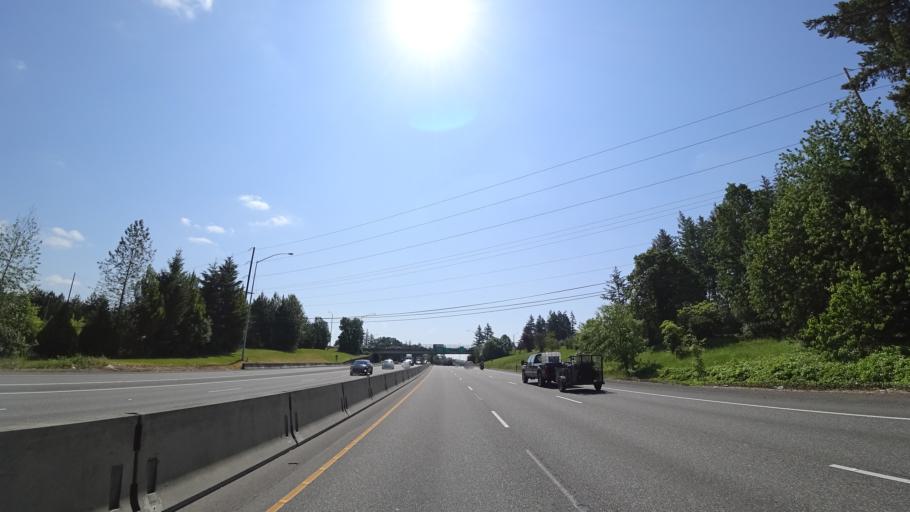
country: US
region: Oregon
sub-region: Washington County
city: Tigard
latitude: 45.4275
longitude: -122.7540
